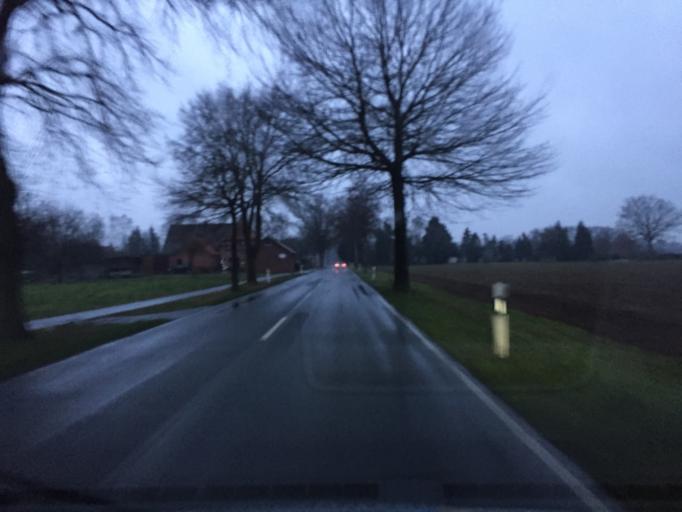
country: DE
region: Lower Saxony
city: Emtinghausen
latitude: 52.9215
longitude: 8.9443
